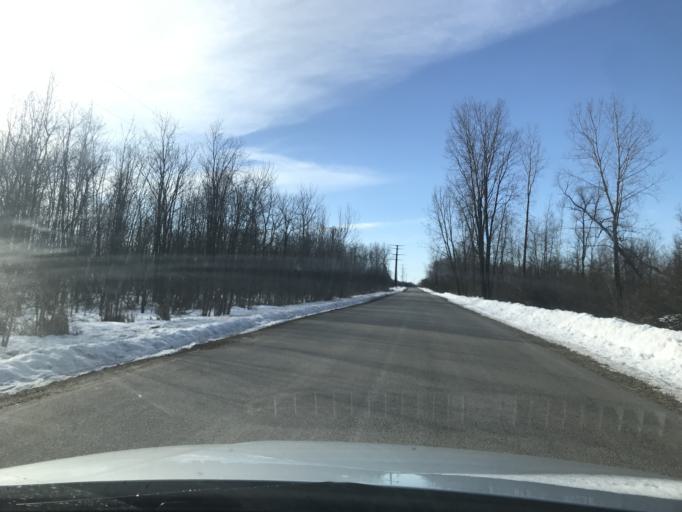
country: US
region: Wisconsin
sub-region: Oconto County
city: Oconto Falls
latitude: 44.9338
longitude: -88.0167
